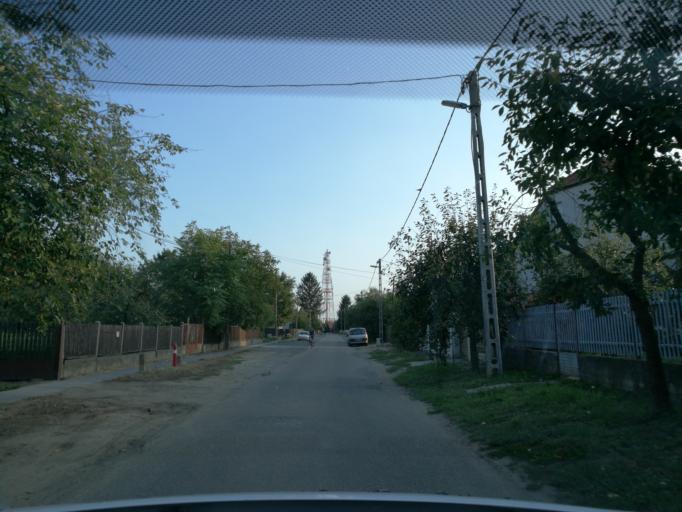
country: HU
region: Szabolcs-Szatmar-Bereg
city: Nyirpazony
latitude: 47.9539
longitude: 21.8016
